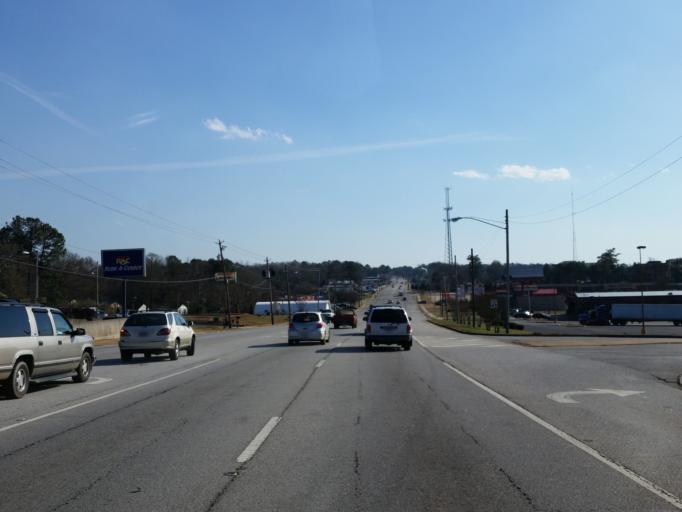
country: US
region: Georgia
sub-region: Spalding County
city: Experiment
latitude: 33.2603
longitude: -84.2889
